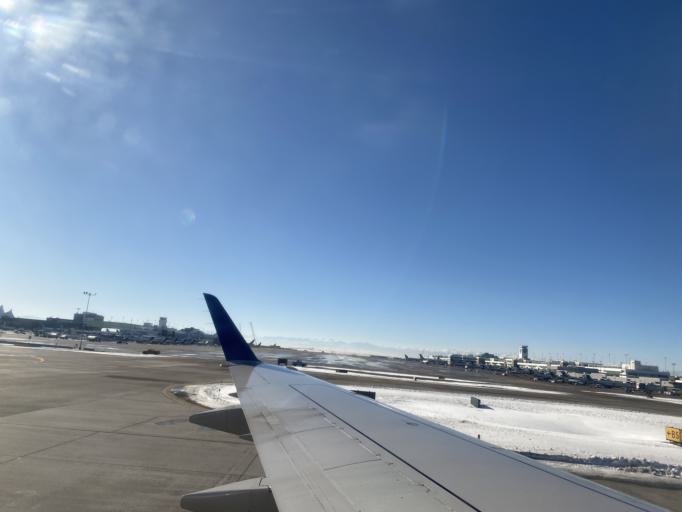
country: US
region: Colorado
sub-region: Weld County
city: Lochbuie
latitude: 39.8560
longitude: -104.6623
